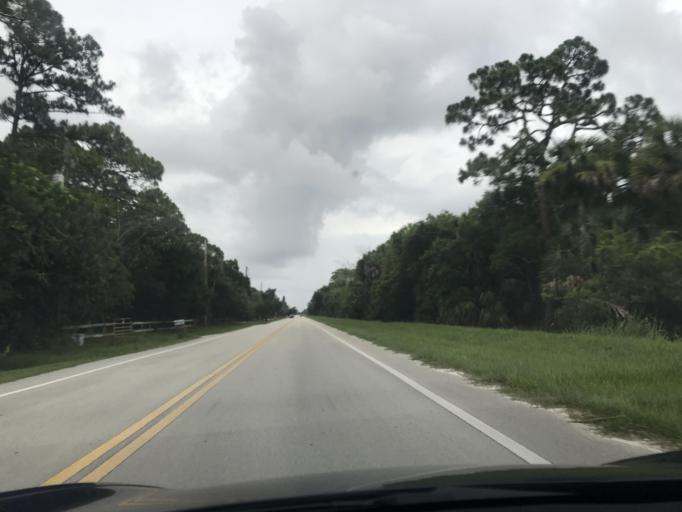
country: US
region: Florida
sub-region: Indian River County
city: West Vero Corridor
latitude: 27.6168
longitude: -80.4570
